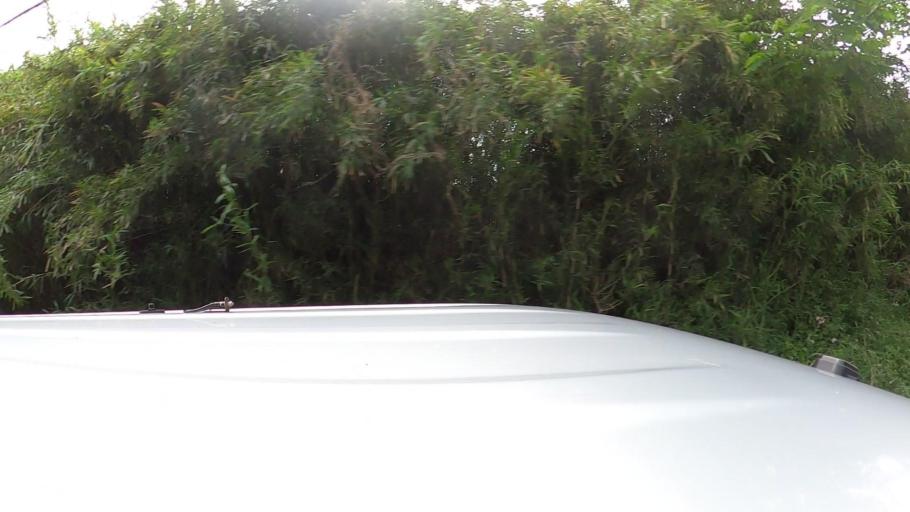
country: JP
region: Ibaraki
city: Ryugasaki
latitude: 35.9579
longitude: 140.2256
